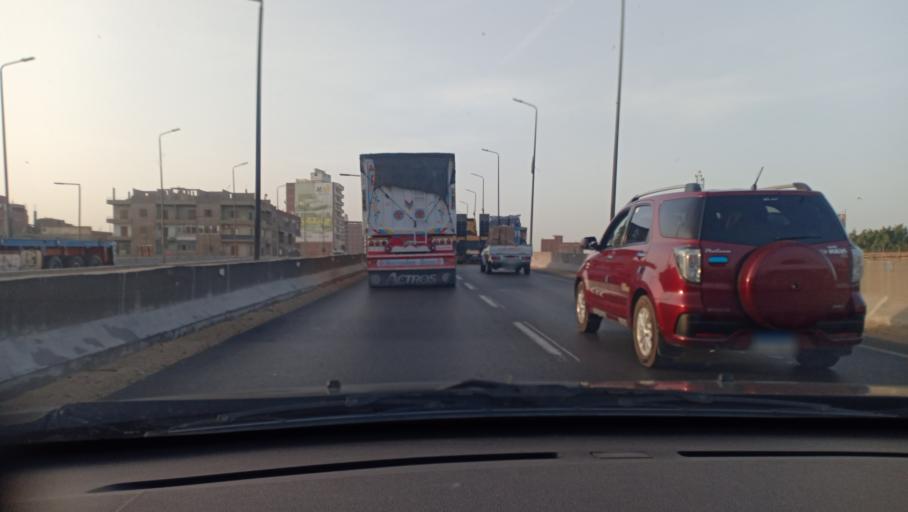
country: EG
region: Muhafazat al Minufiyah
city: Quwaysina
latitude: 30.5472
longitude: 31.2692
